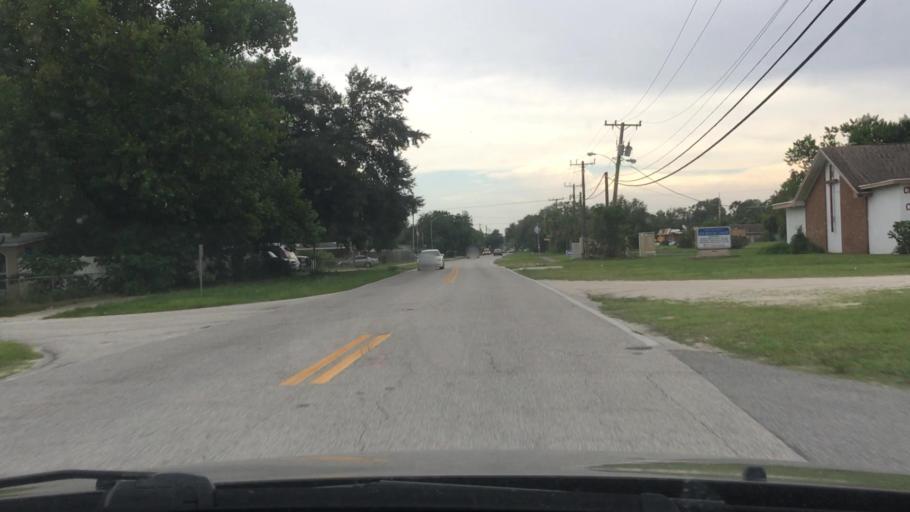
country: US
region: Florida
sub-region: Volusia County
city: Holly Hill
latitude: 29.2343
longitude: -81.0656
